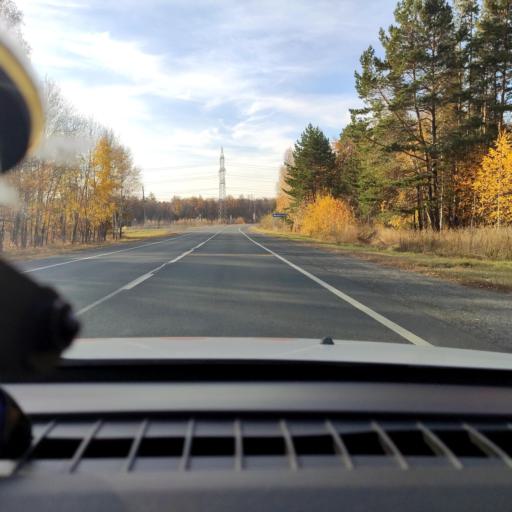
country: RU
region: Samara
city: Volzhskiy
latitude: 53.4528
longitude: 50.1260
